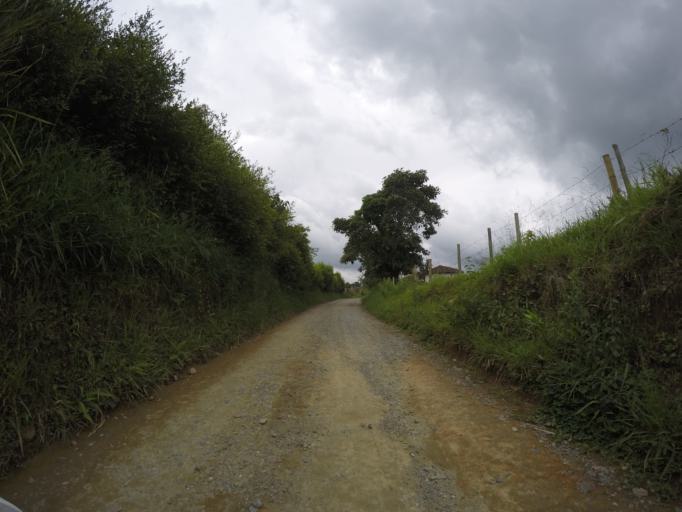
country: CO
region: Quindio
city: Filandia
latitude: 4.6351
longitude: -75.6831
